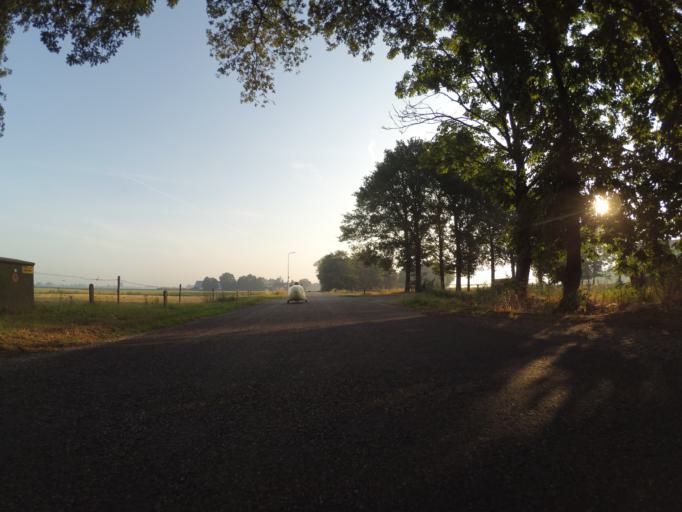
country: NL
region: Overijssel
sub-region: Gemeente Twenterand
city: Magele
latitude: 52.4182
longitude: 6.5282
